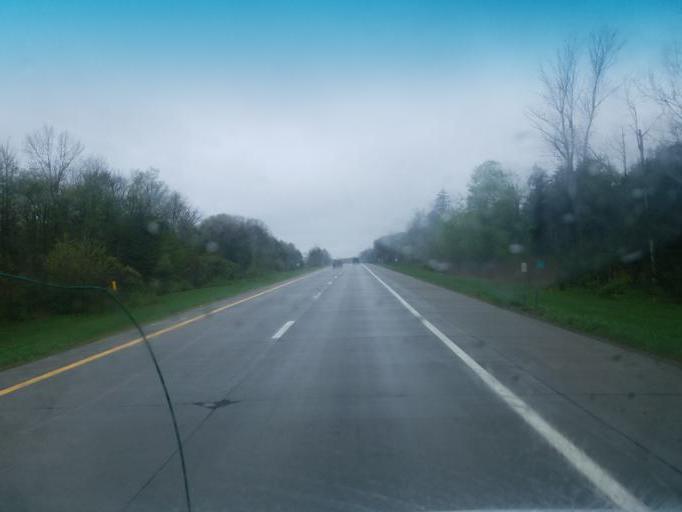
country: US
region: New York
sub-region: Chautauqua County
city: Mayville
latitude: 42.1561
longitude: -79.4597
